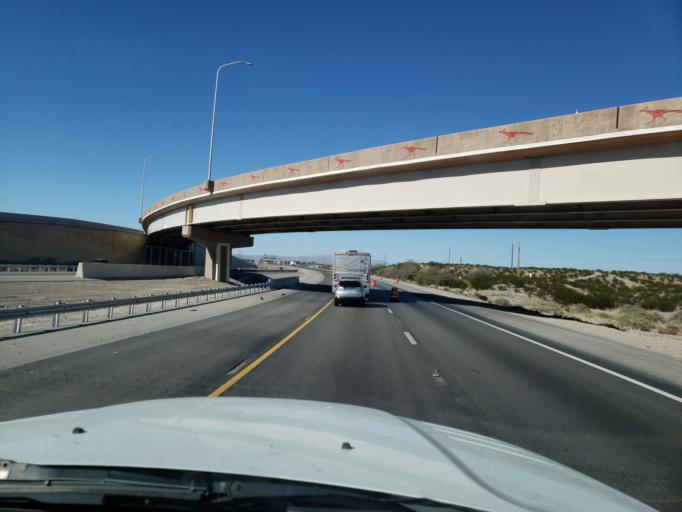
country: US
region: New Mexico
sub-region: Dona Ana County
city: University Park
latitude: 32.2619
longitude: -106.7331
